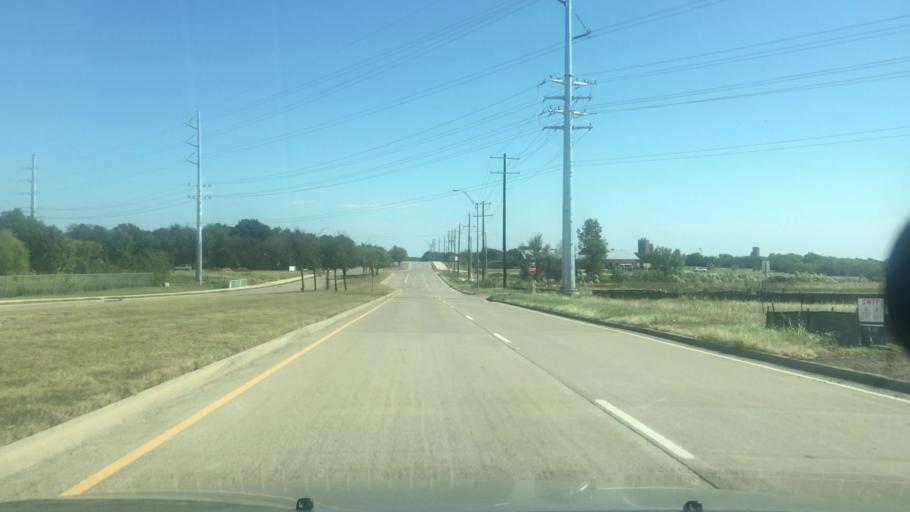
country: US
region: Texas
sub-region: Denton County
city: Denton
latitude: 33.2495
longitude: -97.1503
